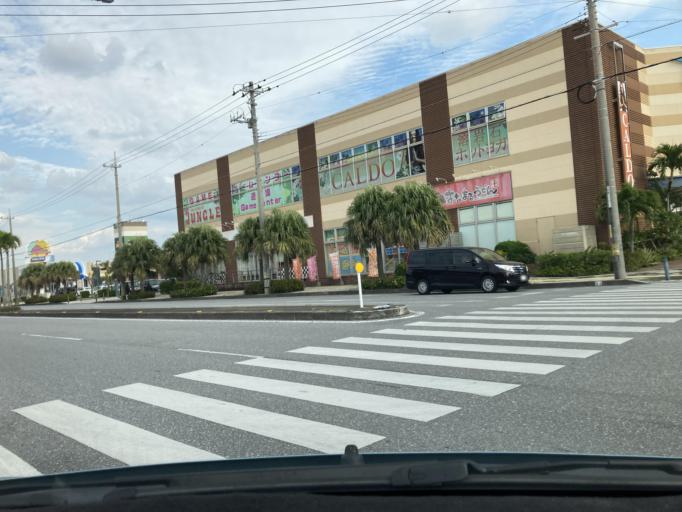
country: JP
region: Okinawa
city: Itoman
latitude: 26.1585
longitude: 127.6587
